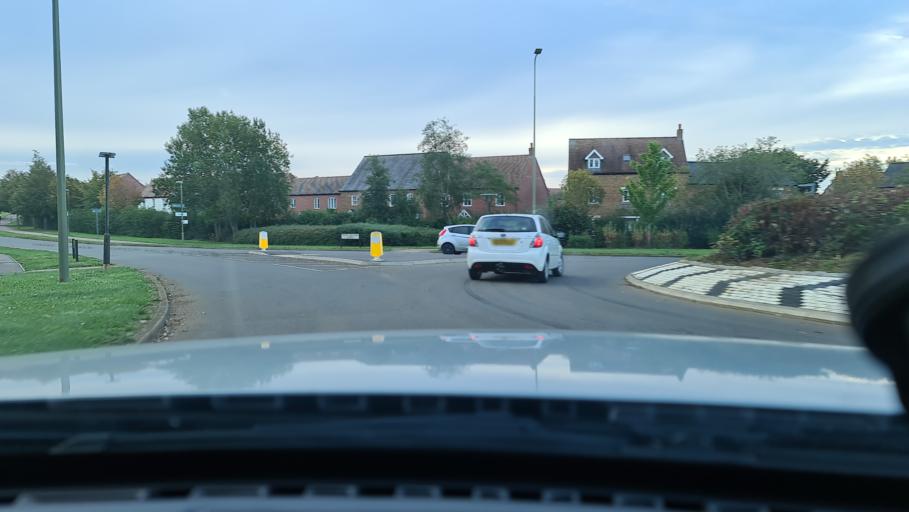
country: GB
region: England
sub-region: Oxfordshire
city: Hanwell
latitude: 52.0793
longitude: -1.3680
